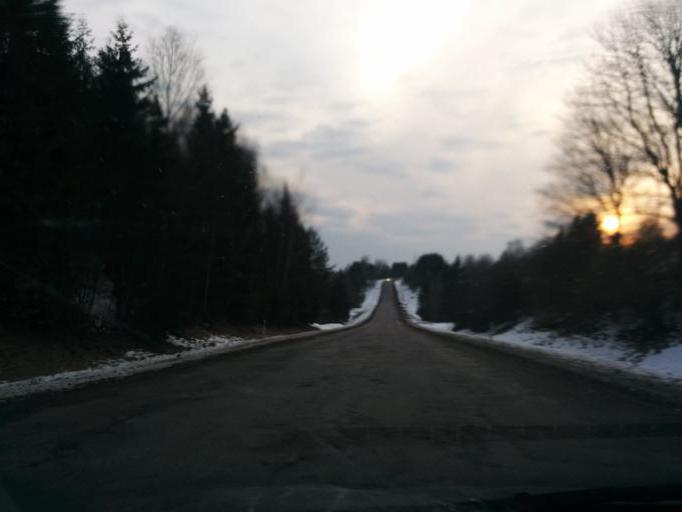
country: LV
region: Priekuli
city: Priekuli
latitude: 57.2721
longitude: 25.4732
